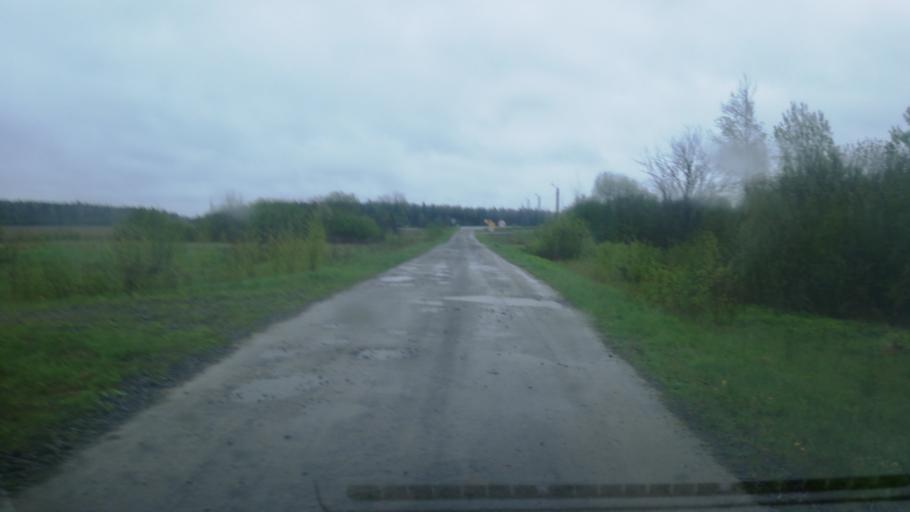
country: RU
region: Jaroslavl
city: Danilov
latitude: 57.9931
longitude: 40.1813
